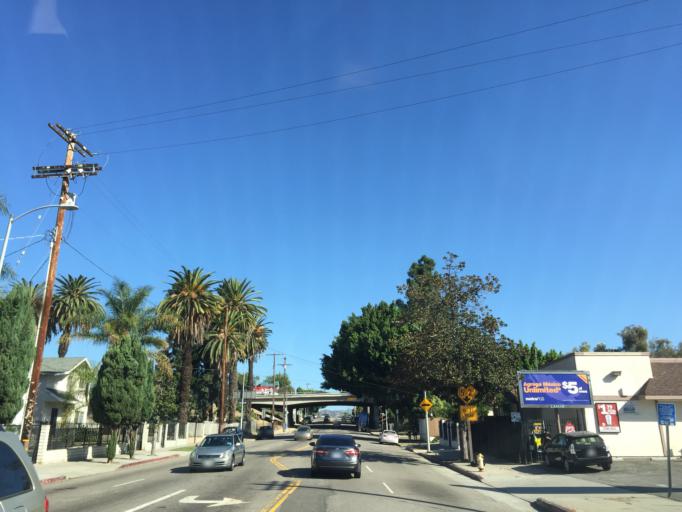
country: US
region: California
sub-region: Los Angeles County
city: Silver Lake
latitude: 34.0767
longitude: -118.2868
